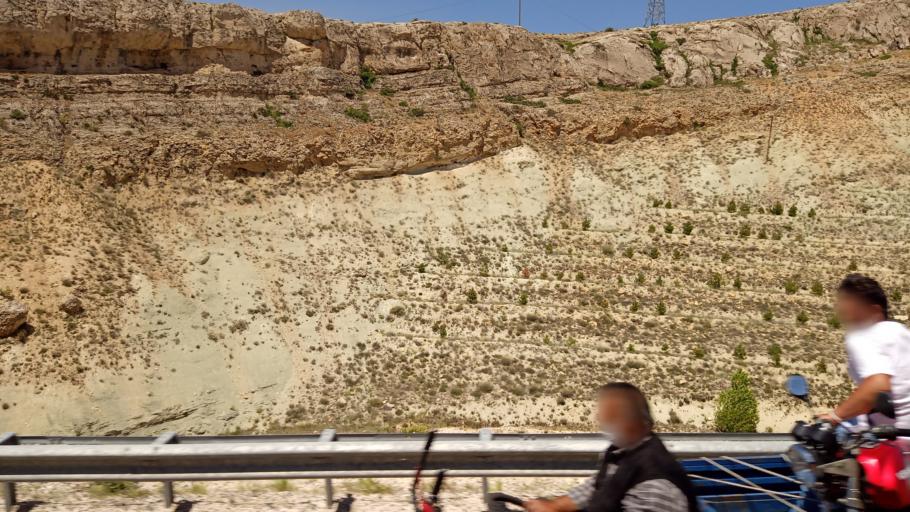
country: TR
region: Malatya
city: Darende
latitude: 38.5752
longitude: 37.4635
